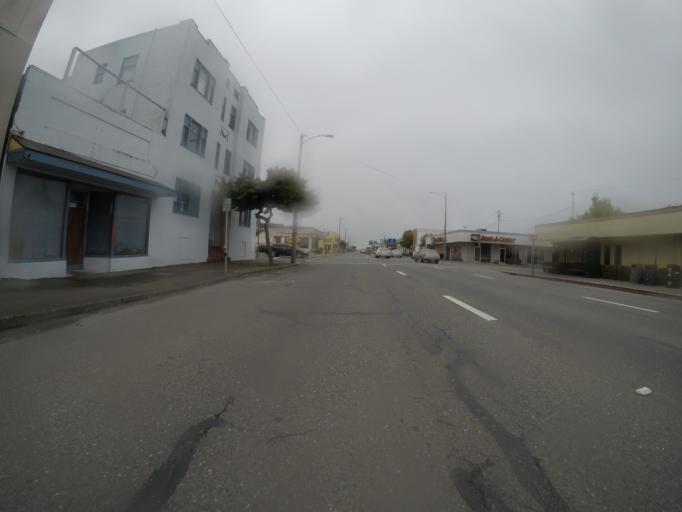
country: US
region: California
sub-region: Humboldt County
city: Eureka
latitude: 40.8025
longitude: -124.1679
